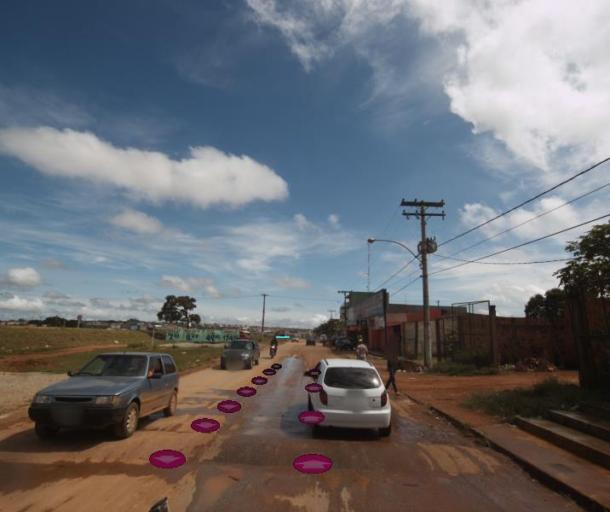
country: BR
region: Federal District
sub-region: Brasilia
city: Brasilia
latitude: -15.7492
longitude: -48.2619
